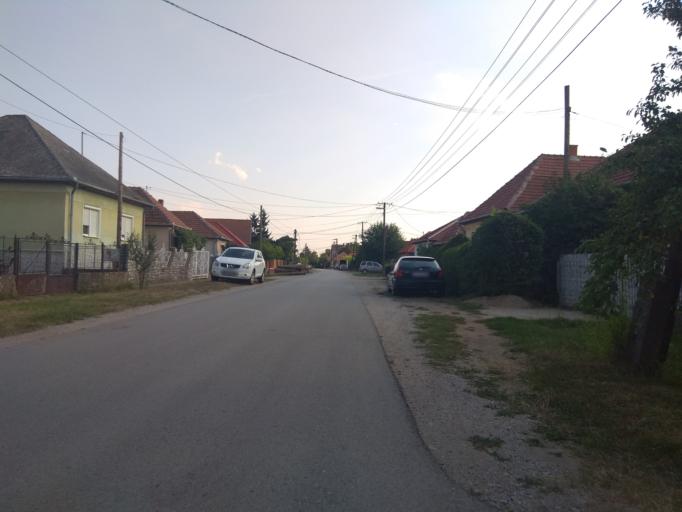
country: HU
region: Borsod-Abauj-Zemplen
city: Mezokeresztes
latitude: 47.8834
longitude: 20.6853
